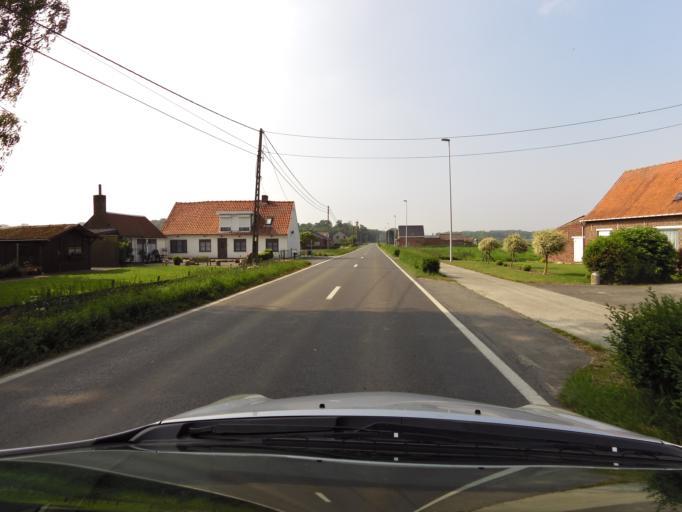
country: BE
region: Flanders
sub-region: Provincie West-Vlaanderen
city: Poperinge
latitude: 50.8759
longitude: 2.7059
